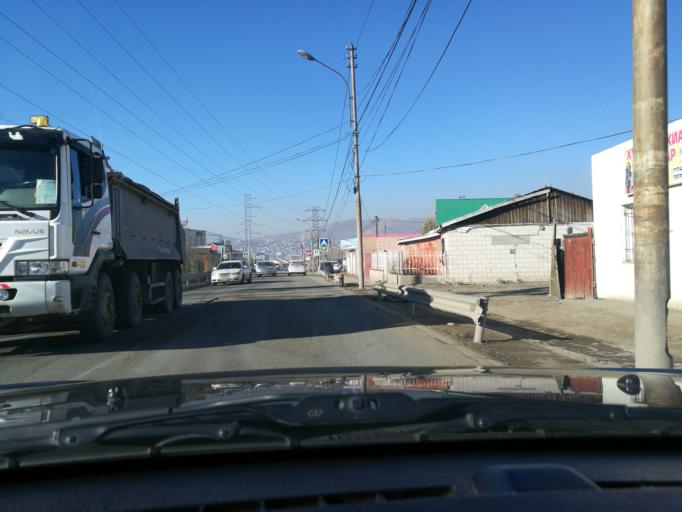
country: MN
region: Ulaanbaatar
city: Ulaanbaatar
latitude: 47.9790
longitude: 106.9339
